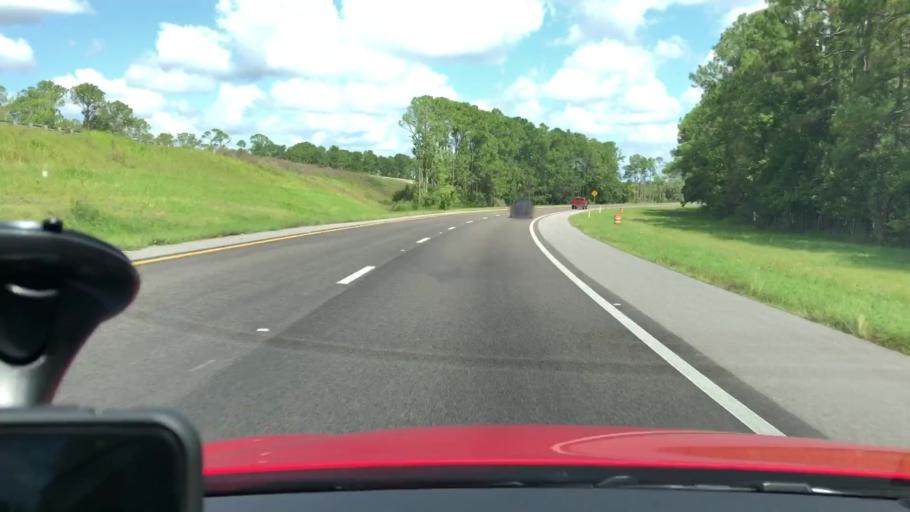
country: US
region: Florida
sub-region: Volusia County
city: Samsula-Spruce Creek
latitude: 29.1421
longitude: -81.1183
